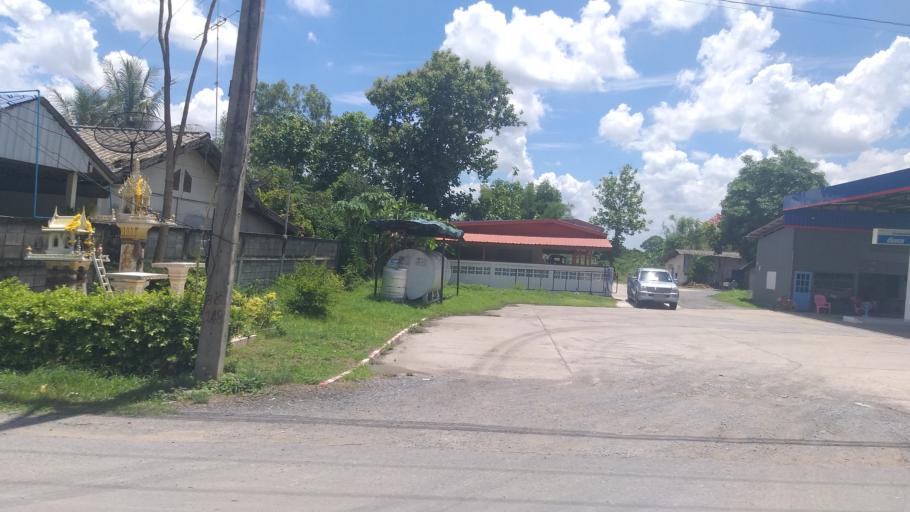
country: TH
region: Nakhon Nayok
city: Ban Na
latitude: 14.2896
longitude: 101.0675
